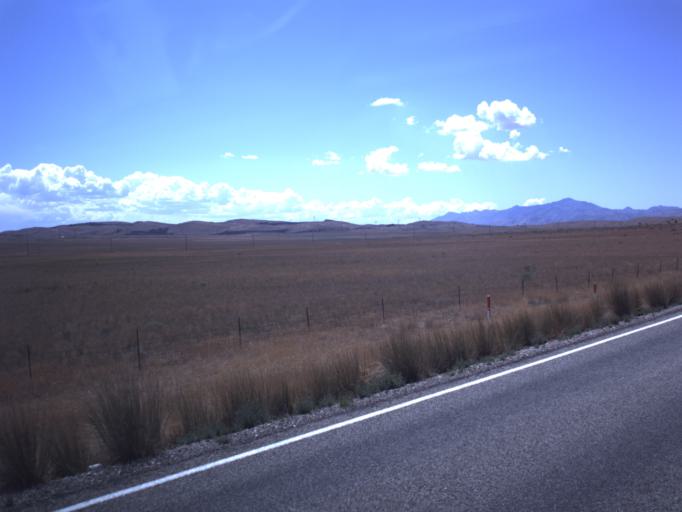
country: US
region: Utah
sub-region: Juab County
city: Nephi
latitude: 39.6726
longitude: -112.0272
